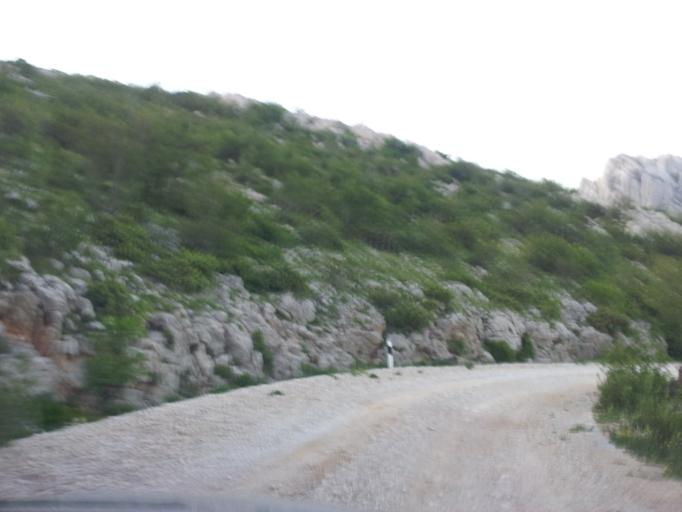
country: HR
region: Zadarska
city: Obrovac
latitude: 44.2556
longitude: 15.6366
